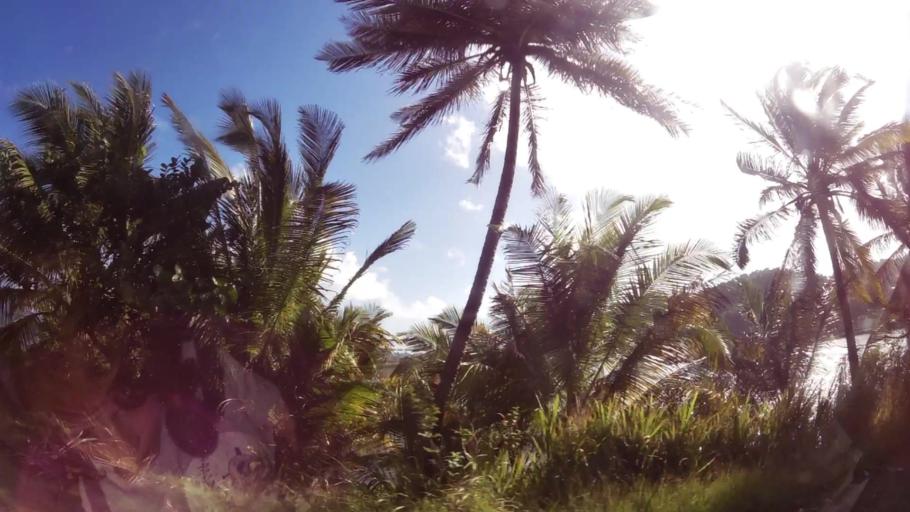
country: DM
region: Saint Andrew
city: Marigot
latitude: 15.5436
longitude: -61.2877
